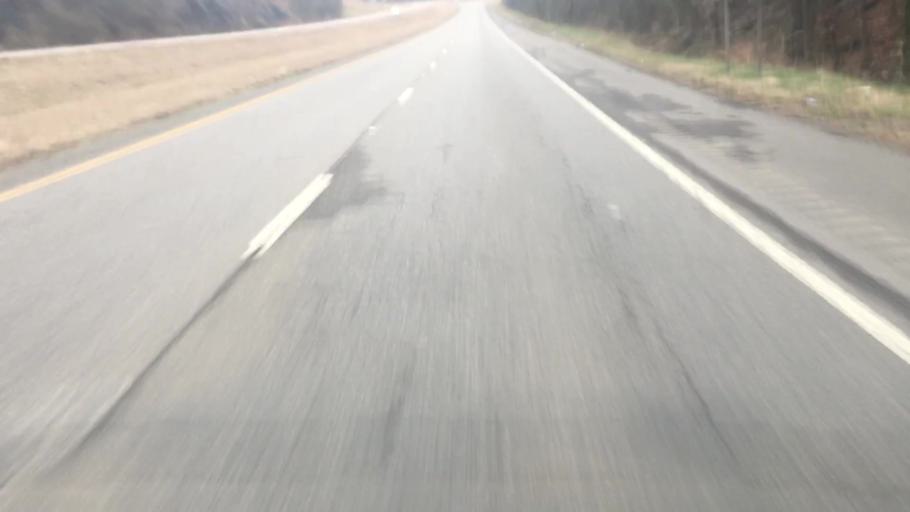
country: US
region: Alabama
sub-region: Walker County
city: Sumiton
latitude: 33.7768
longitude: -87.0798
